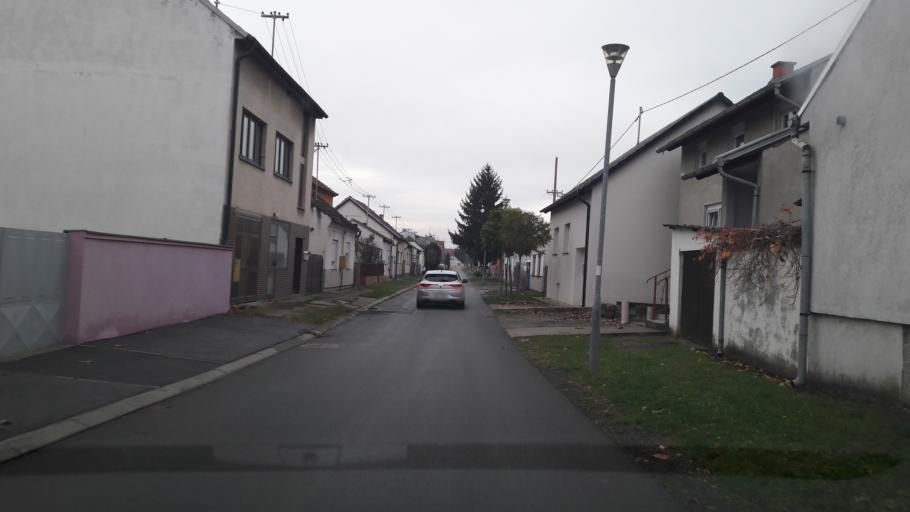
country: HR
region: Osjecko-Baranjska
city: Visnjevac
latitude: 45.5669
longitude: 18.6177
